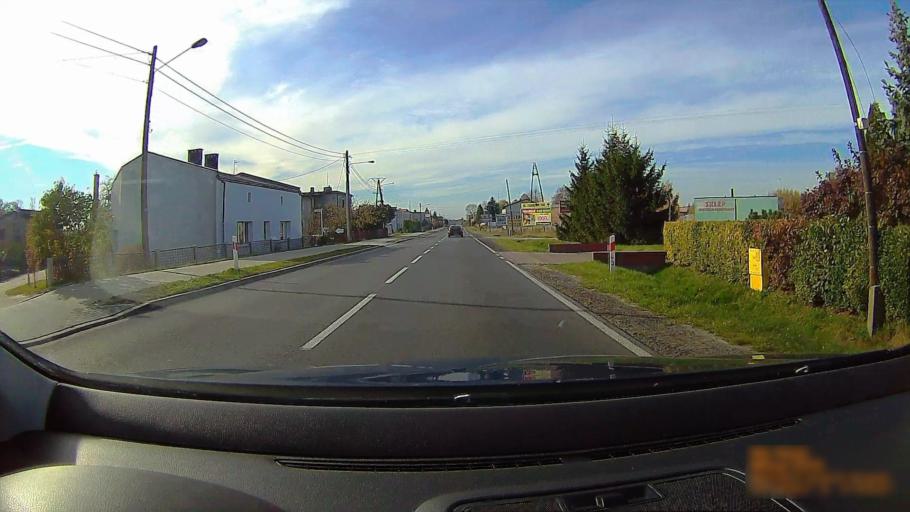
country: PL
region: Greater Poland Voivodeship
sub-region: Powiat ostrzeszowski
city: Ostrzeszow
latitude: 51.4301
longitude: 17.9520
